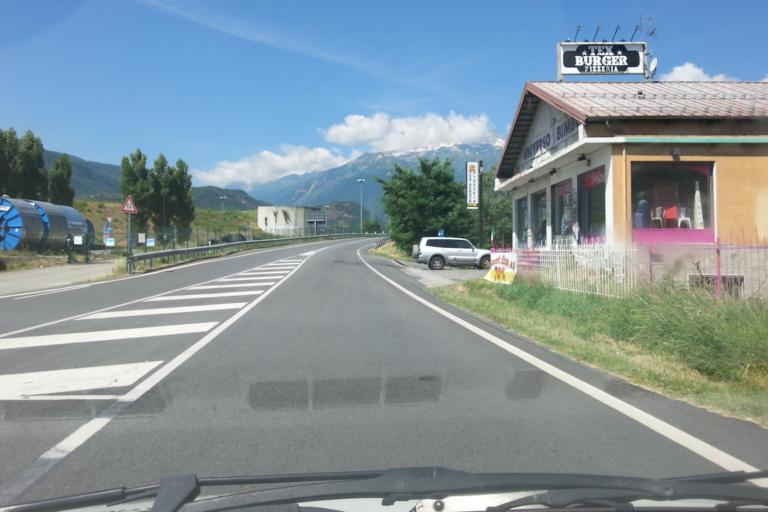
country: IT
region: Piedmont
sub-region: Provincia di Torino
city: Susa
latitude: 45.1381
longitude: 7.0786
